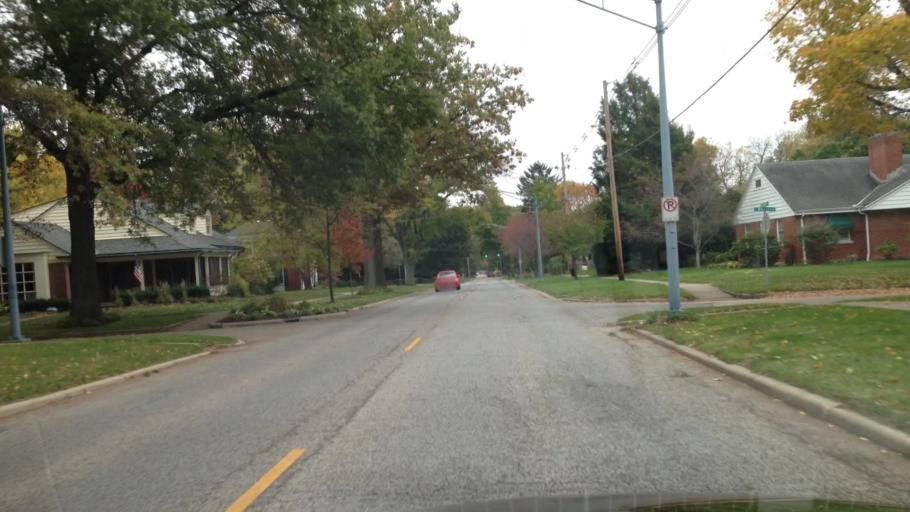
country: US
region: Illinois
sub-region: Champaign County
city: Champaign
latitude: 40.1101
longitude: -88.2605
